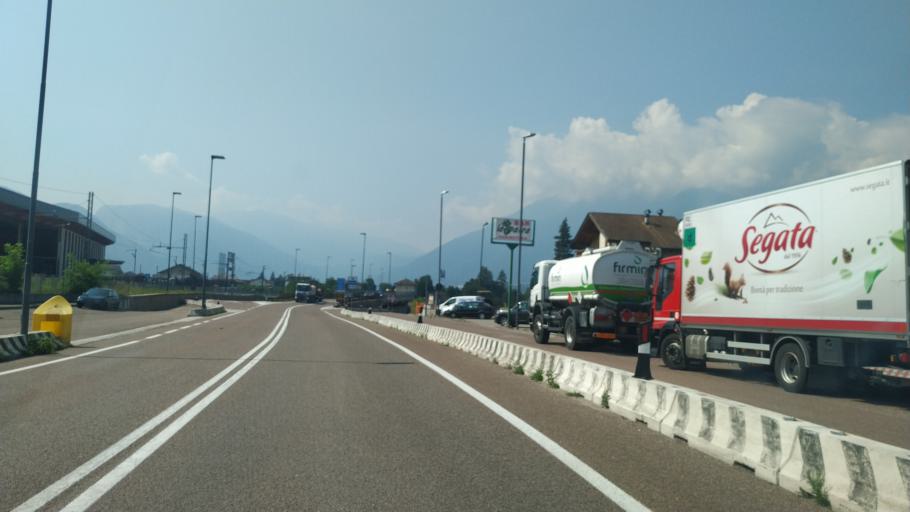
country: IT
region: Trentino-Alto Adige
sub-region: Provincia di Trento
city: Taio
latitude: 46.2994
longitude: 11.0696
